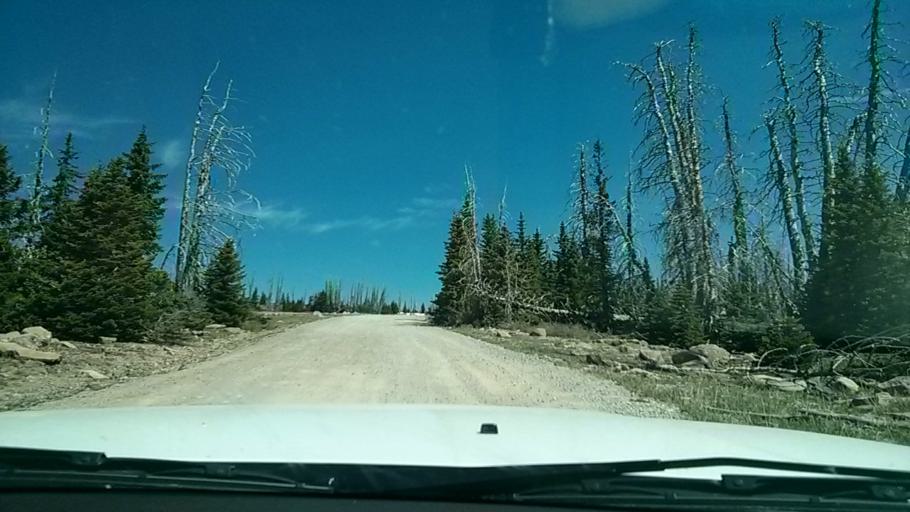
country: US
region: Utah
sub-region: Iron County
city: Parowan
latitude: 37.6832
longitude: -112.8195
